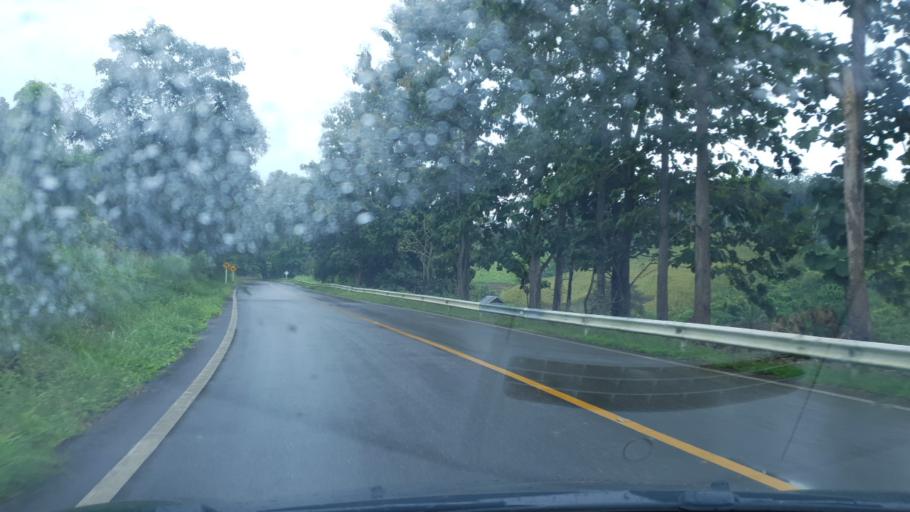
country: TH
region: Mae Hong Son
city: Mae La Noi
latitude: 18.5165
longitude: 97.9277
